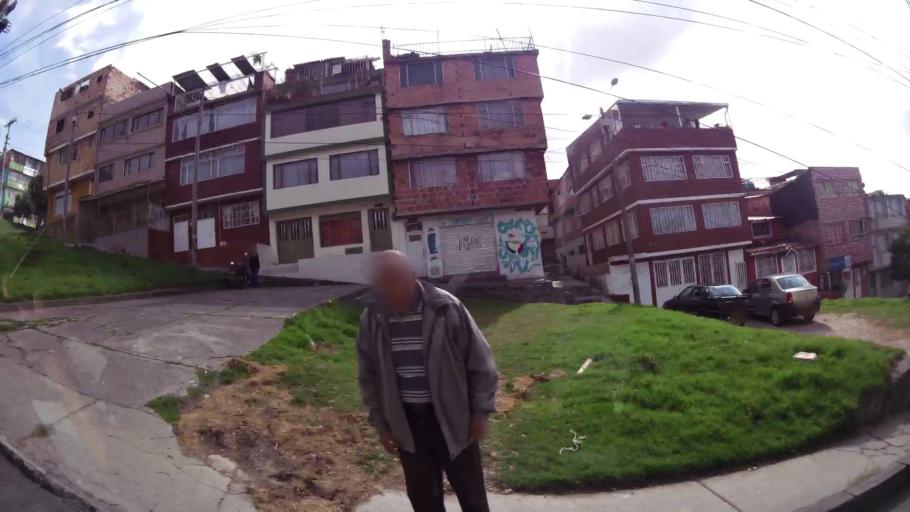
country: CO
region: Bogota D.C.
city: Bogota
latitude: 4.5569
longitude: -74.0979
